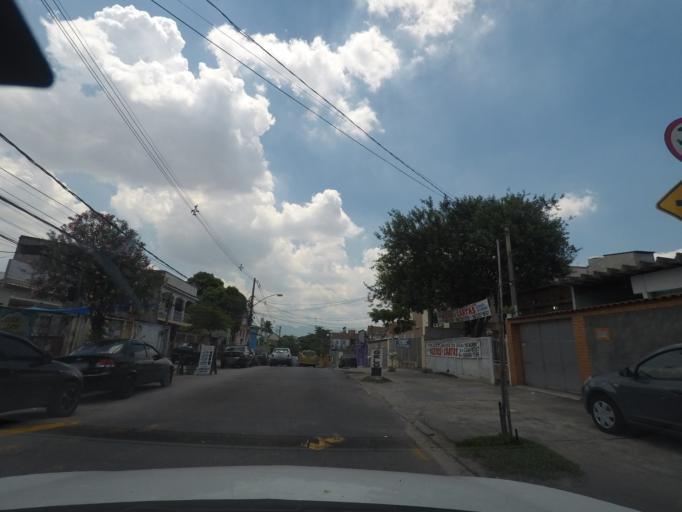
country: BR
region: Rio de Janeiro
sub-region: Sao Joao De Meriti
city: Sao Joao de Meriti
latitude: -22.8627
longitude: -43.3637
